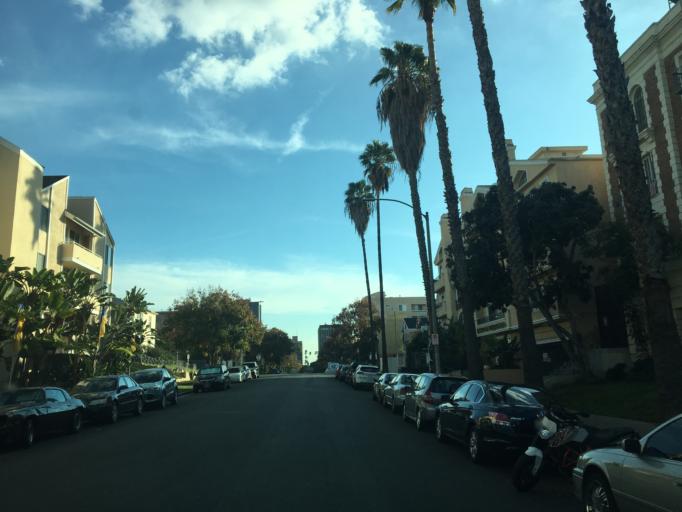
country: US
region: California
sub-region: Los Angeles County
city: Silver Lake
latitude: 34.0680
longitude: -118.2941
